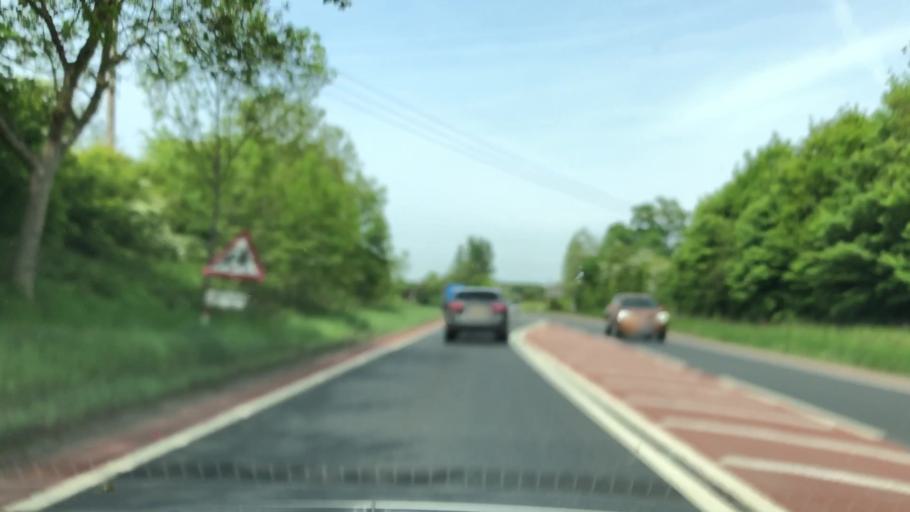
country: GB
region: England
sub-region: Shropshire
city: Gobowen
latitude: 52.9102
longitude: -3.0423
